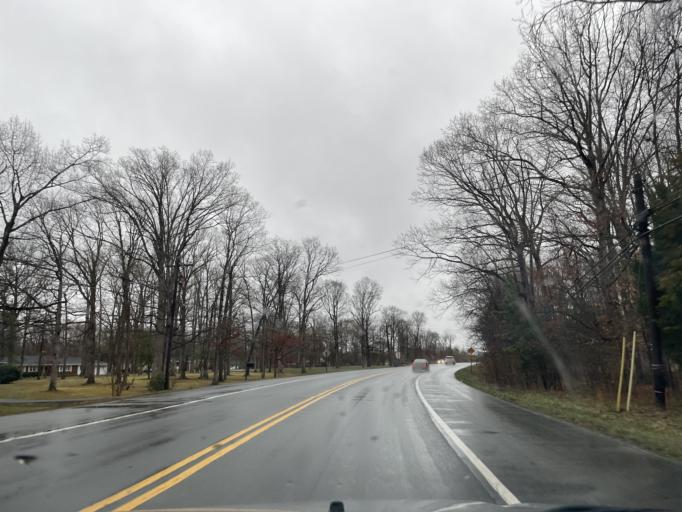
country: US
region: Maryland
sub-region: Charles County
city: La Plata
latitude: 38.5309
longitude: -76.9584
